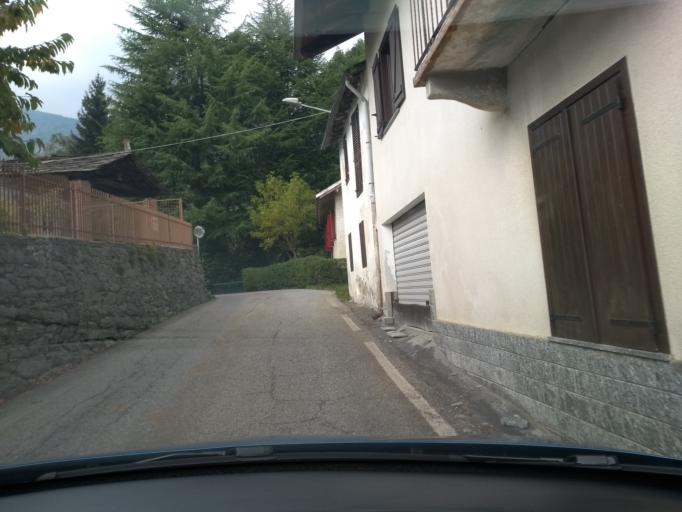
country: IT
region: Piedmont
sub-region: Provincia di Torino
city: Corio
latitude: 45.3176
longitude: 7.5207
